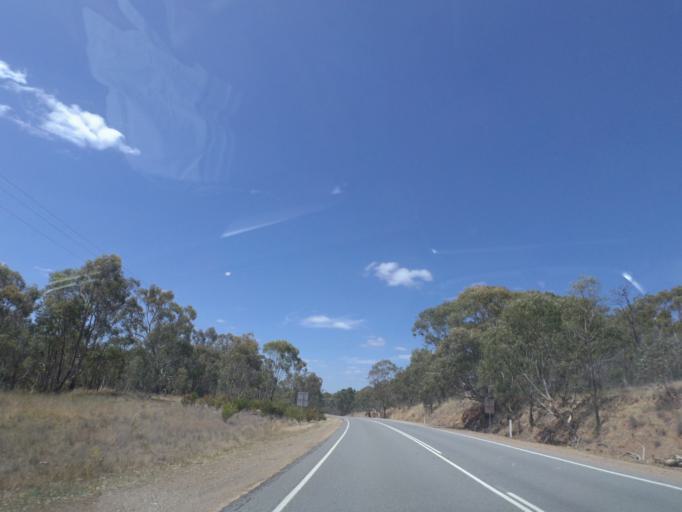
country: AU
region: Victoria
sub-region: Wangaratta
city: Wangaratta
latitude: -36.4610
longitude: 146.2325
